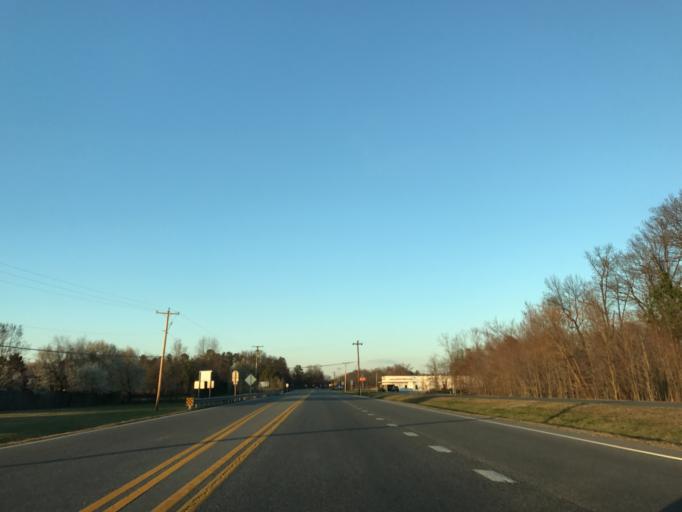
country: US
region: Maryland
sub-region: Talbot County
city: Easton
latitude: 38.7956
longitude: -76.0643
